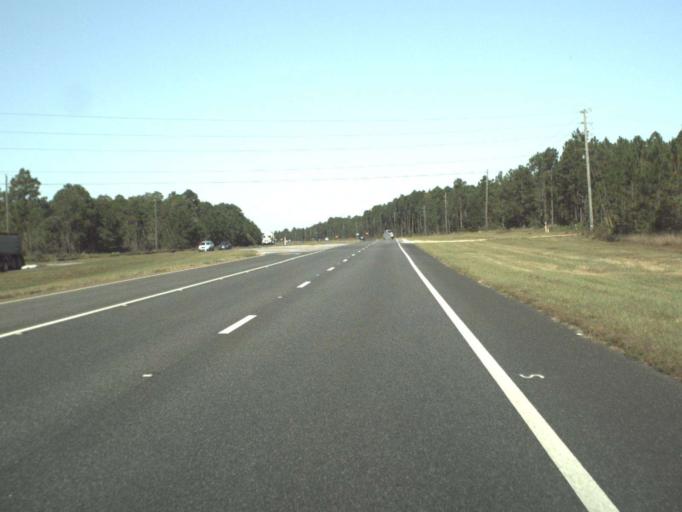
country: US
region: Florida
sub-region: Walton County
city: Seaside
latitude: 30.3473
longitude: -86.0777
